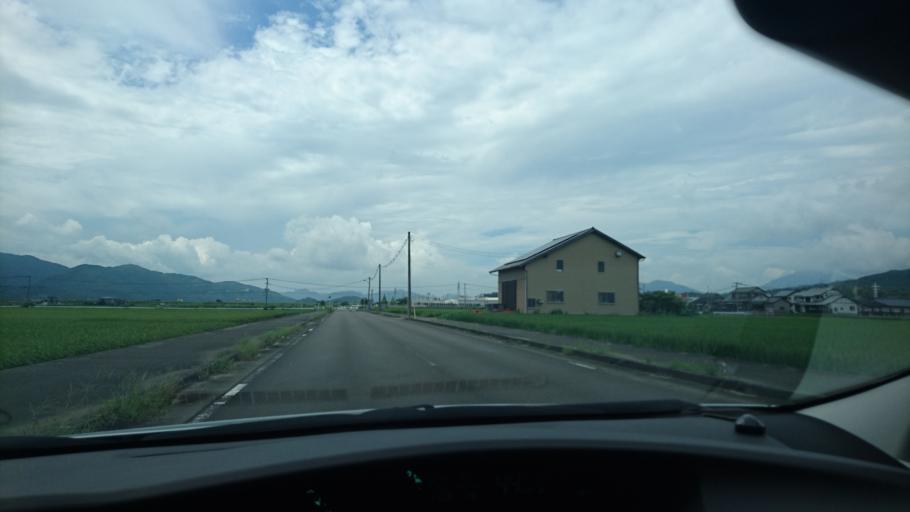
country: JP
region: Saga Prefecture
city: Takeocho-takeo
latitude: 33.2103
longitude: 130.1176
